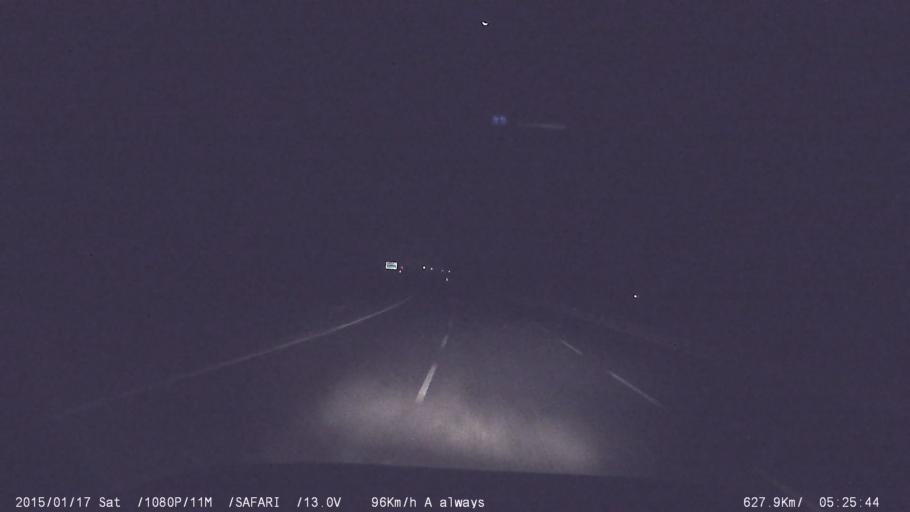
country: IN
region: Tamil Nadu
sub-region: Vellore
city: Arcot
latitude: 12.9409
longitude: 79.2370
